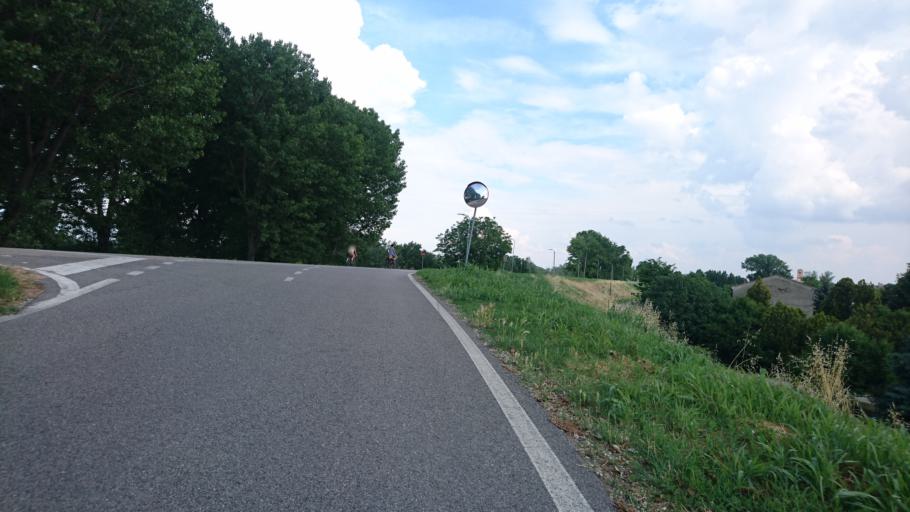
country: IT
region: Lombardy
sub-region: Provincia di Mantova
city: Sermide
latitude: 45.0126
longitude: 11.2922
